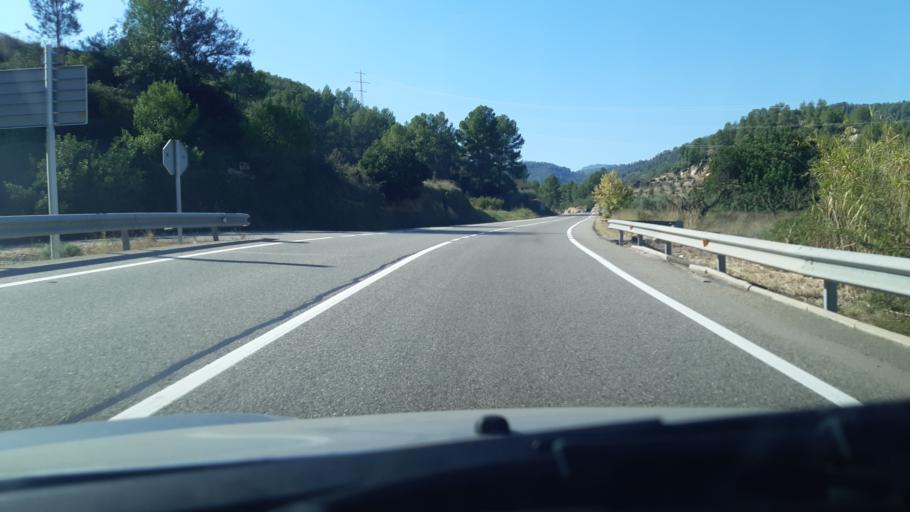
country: ES
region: Catalonia
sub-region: Provincia de Tarragona
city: Benifallet
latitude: 40.9819
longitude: 0.5336
